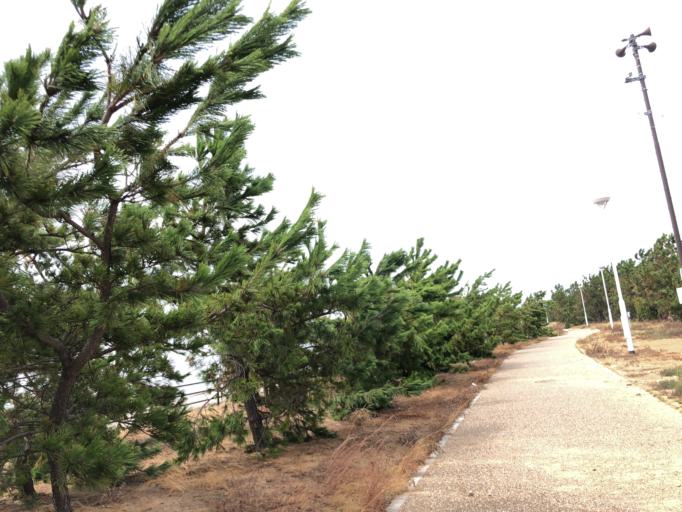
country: JP
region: Hyogo
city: Nishinomiya-hama
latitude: 34.7052
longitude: 135.3205
